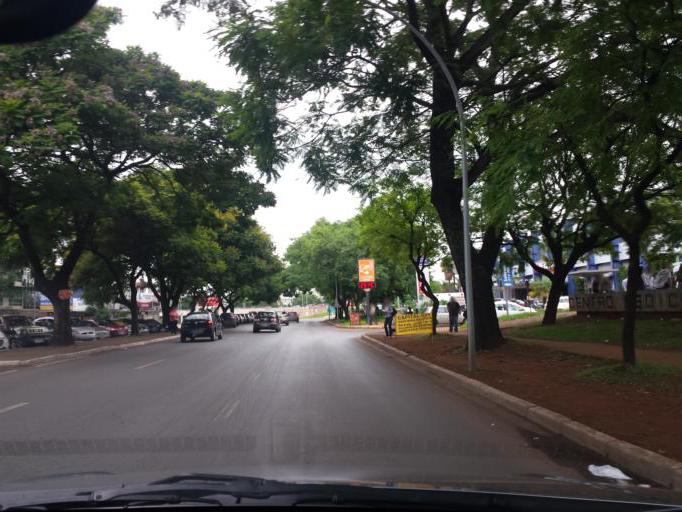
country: BR
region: Federal District
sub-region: Brasilia
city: Brasilia
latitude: -15.8282
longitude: -47.9284
